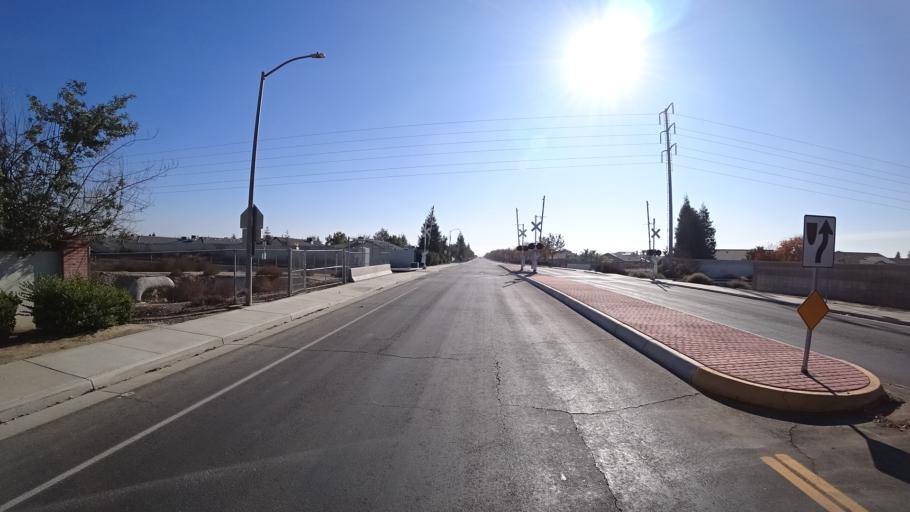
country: US
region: California
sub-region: Kern County
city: Greenacres
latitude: 35.3113
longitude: -119.1187
